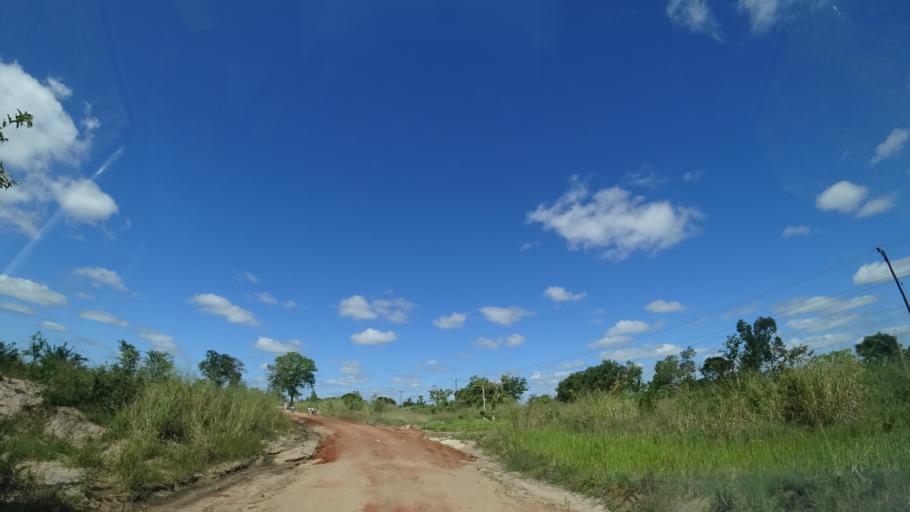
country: MZ
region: Sofala
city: Dondo
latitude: -19.2756
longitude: 34.6807
